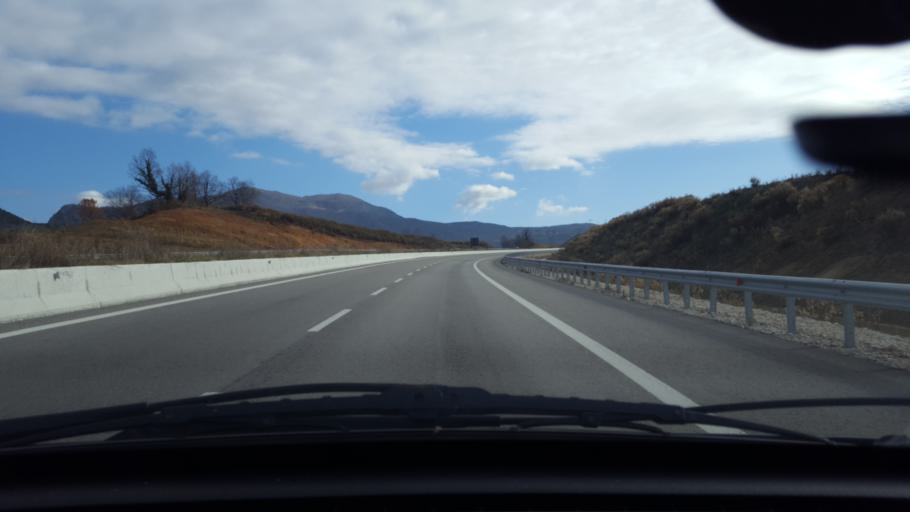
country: AL
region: Tirane
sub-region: Rrethi i Tiranes
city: Krrabe
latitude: 41.2255
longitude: 19.9404
